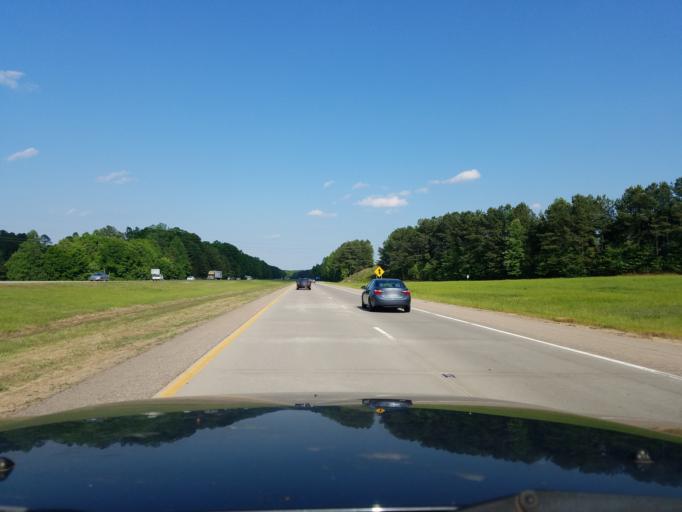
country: US
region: North Carolina
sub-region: Vance County
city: South Henderson
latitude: 36.3207
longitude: -78.4888
